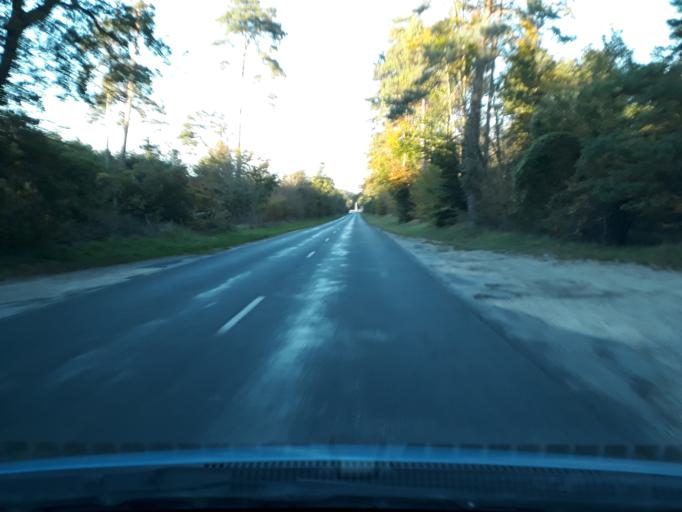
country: FR
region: Ile-de-France
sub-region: Departement de Seine-et-Marne
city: Avon
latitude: 48.4374
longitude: 2.7152
